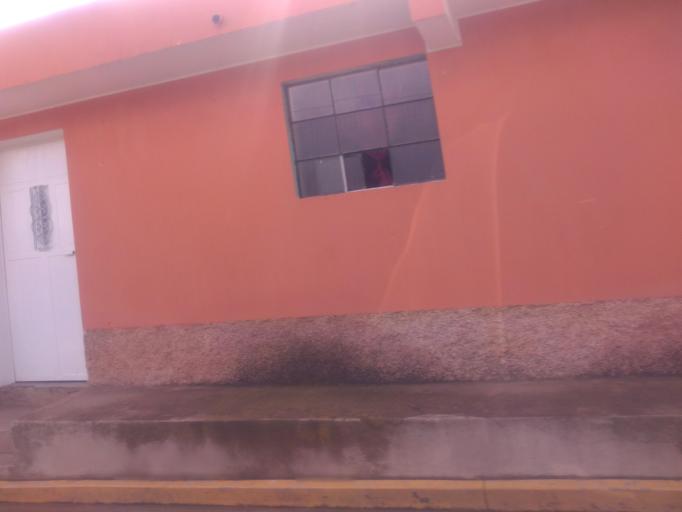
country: GT
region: Quetzaltenango
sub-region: Municipio de La Esperanza
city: La Esperanza
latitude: 14.8614
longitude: -91.5700
